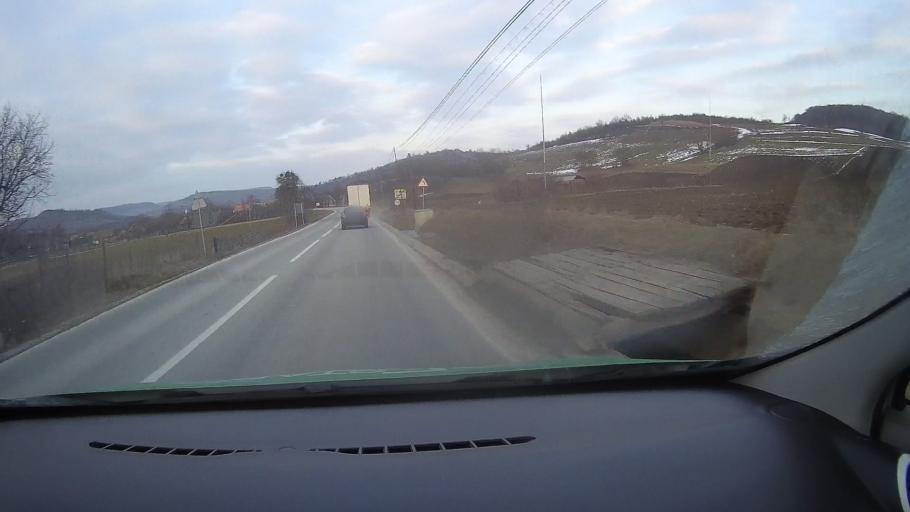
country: RO
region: Harghita
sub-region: Comuna Simonesti
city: Simonesti
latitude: 46.3438
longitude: 25.1165
